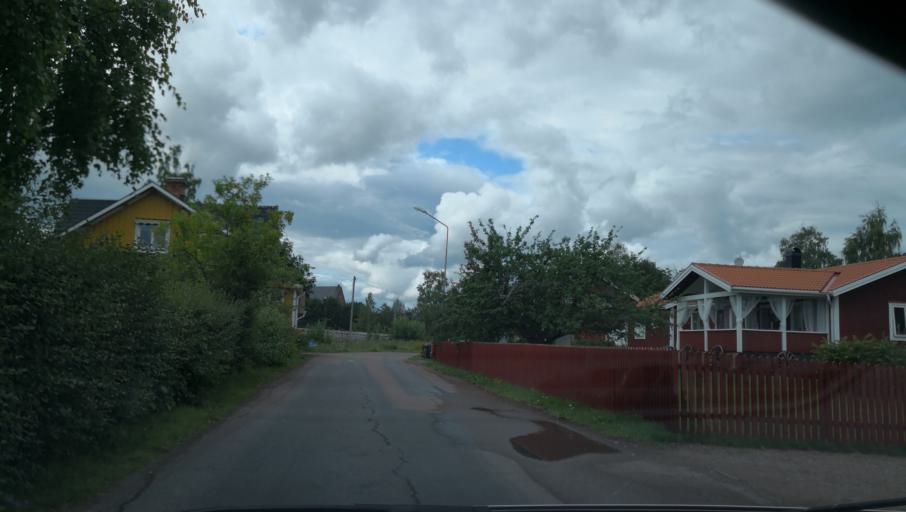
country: SE
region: Dalarna
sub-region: Borlange Kommun
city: Ornas
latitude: 60.4623
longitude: 15.5737
